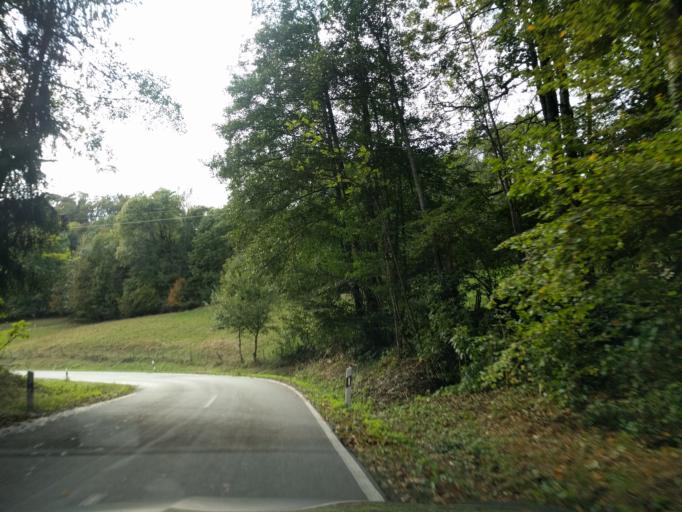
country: DE
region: Bavaria
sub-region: Lower Bavaria
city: Grafling
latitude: 48.8722
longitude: 12.9861
